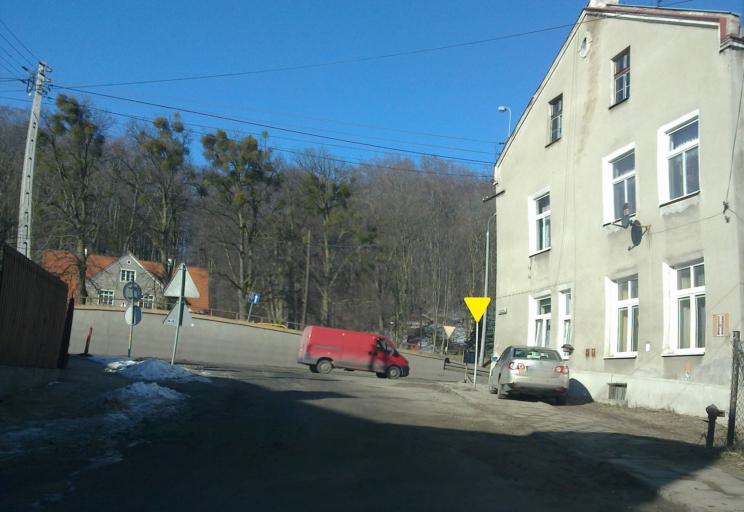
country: PL
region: Pomeranian Voivodeship
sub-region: Powiat gdanski
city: Rotmanka
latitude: 54.3022
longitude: 18.6317
